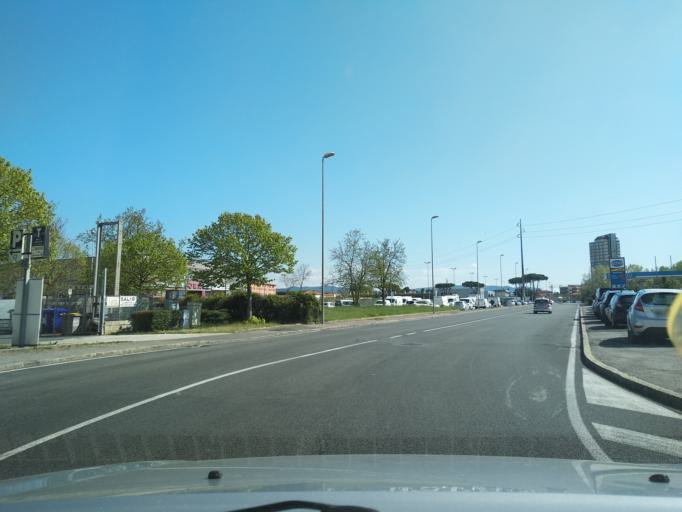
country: IT
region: Tuscany
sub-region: Provincia di Livorno
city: Livorno
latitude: 43.5663
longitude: 10.3420
